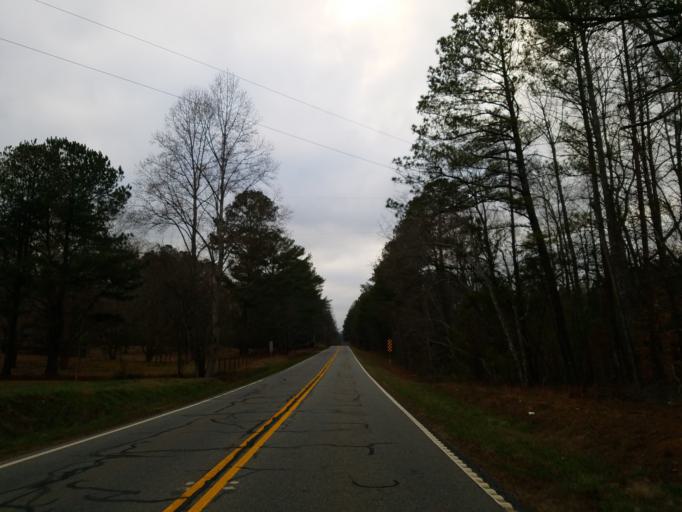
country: US
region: Georgia
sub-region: Bartow County
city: Rydal
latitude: 34.3414
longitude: -84.6226
